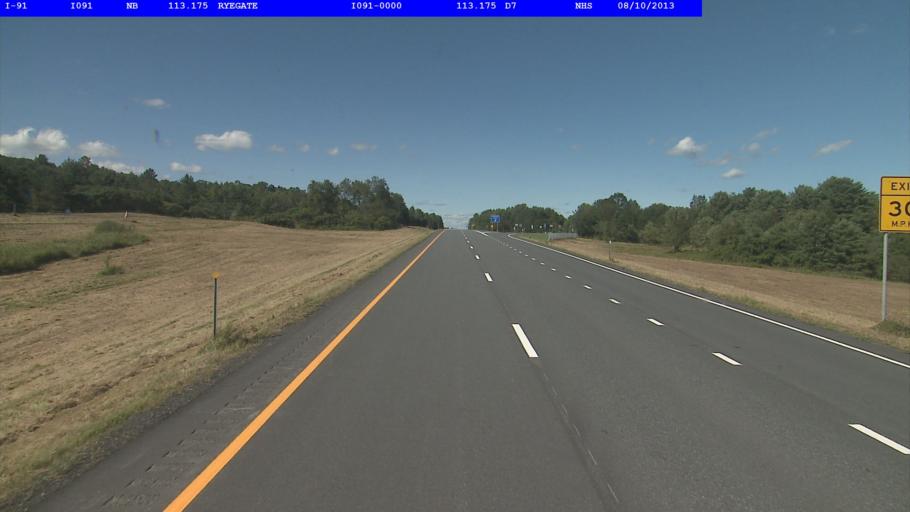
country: US
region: New Hampshire
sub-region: Grafton County
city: Woodsville
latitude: 44.1987
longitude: -72.0709
